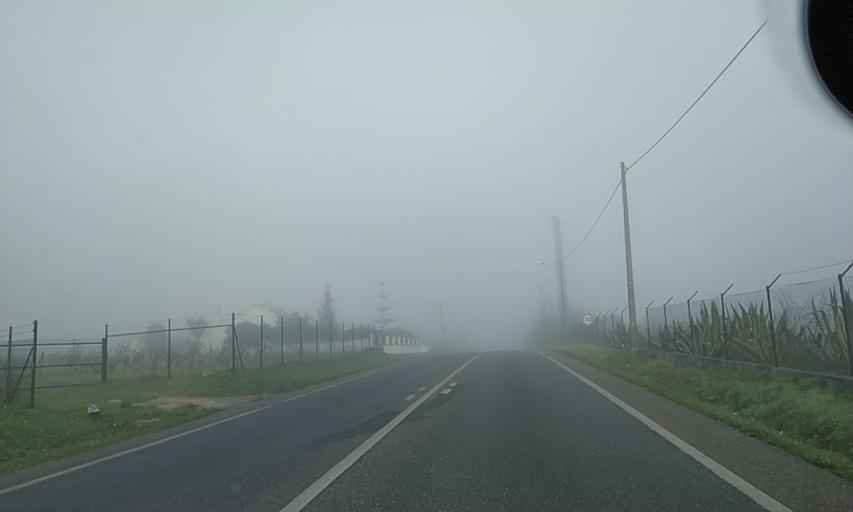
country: PT
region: Setubal
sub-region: Palmela
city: Pinhal Novo
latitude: 38.6175
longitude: -8.9140
